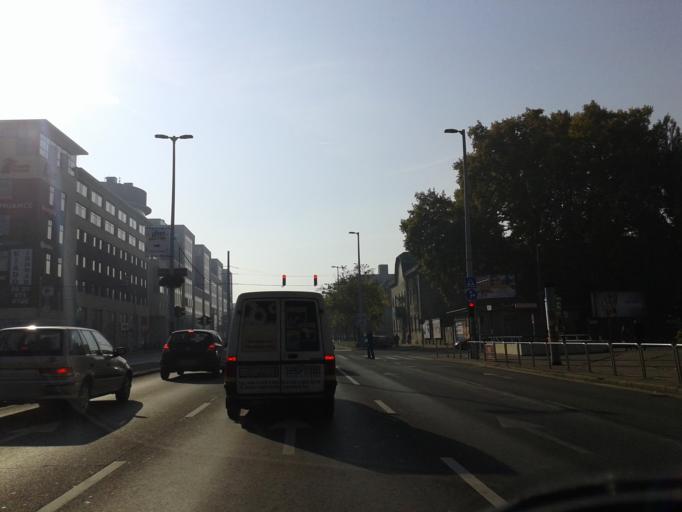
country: HU
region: Budapest
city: Budapest IV. keruelet
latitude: 47.5489
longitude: 19.0732
